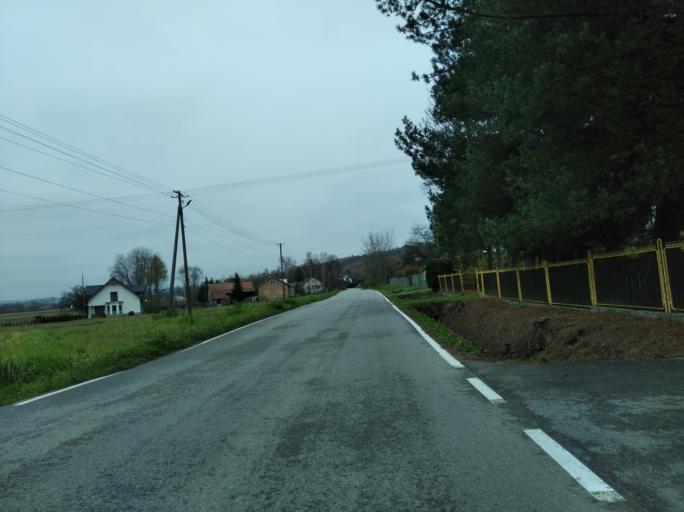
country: PL
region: Subcarpathian Voivodeship
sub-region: Powiat krosnienski
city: Leki
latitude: 49.8142
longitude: 21.6533
